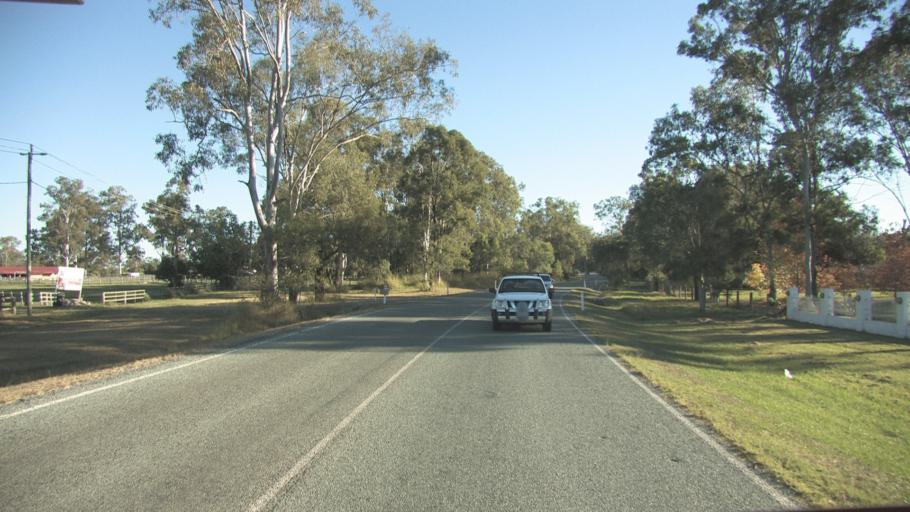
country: AU
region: Queensland
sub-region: Logan
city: Chambers Flat
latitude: -27.7488
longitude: 153.0580
